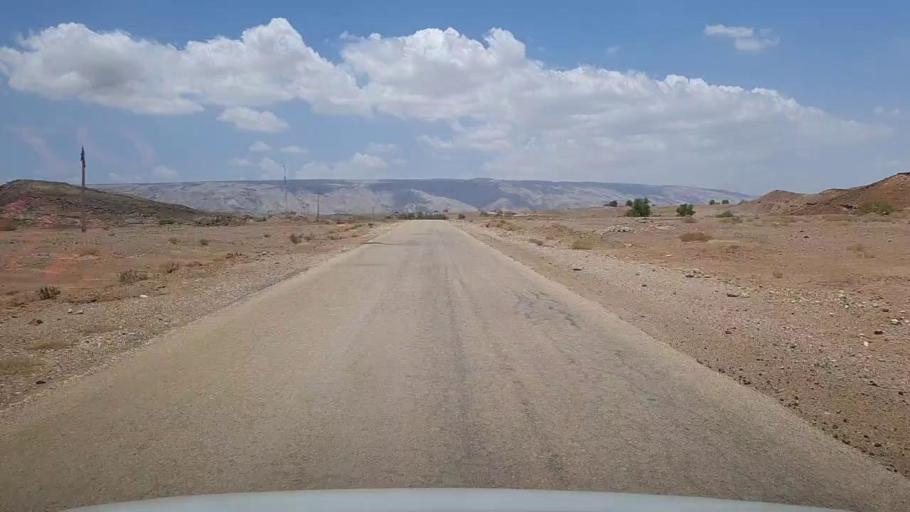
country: PK
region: Sindh
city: Bhan
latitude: 26.3187
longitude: 67.5577
